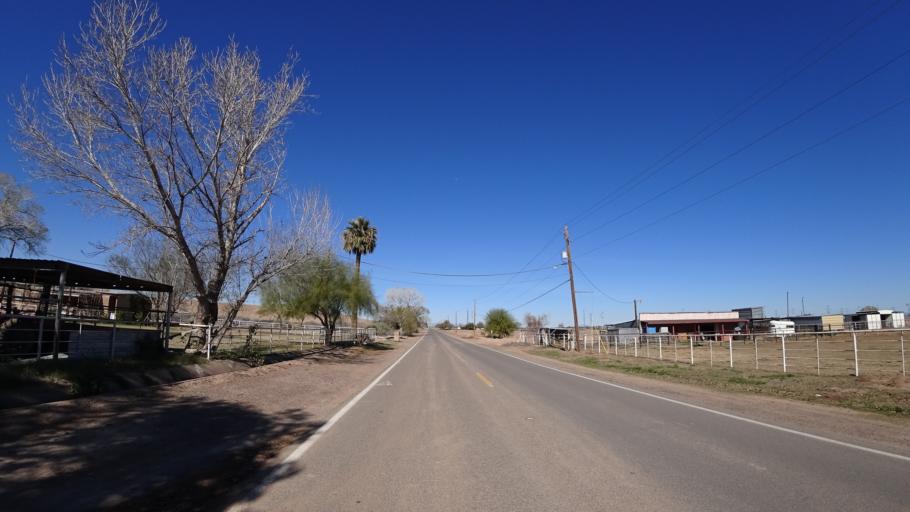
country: US
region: Arizona
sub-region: Maricopa County
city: Avondale
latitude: 33.3950
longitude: -112.3405
